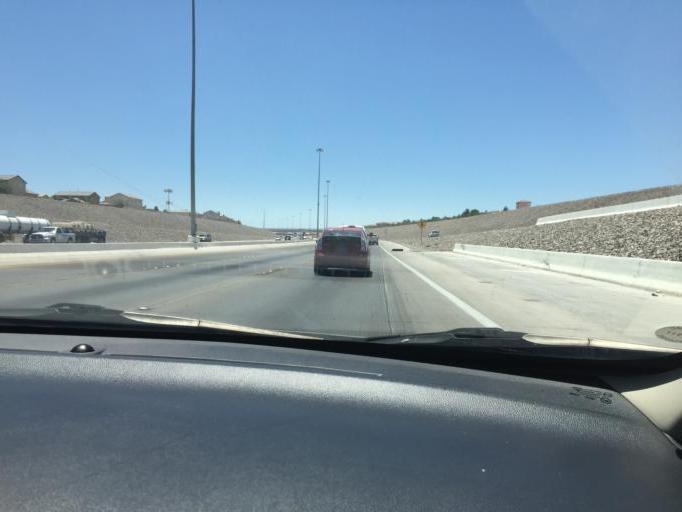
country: US
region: Nevada
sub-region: Clark County
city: Paradise
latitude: 36.0417
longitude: -115.1342
